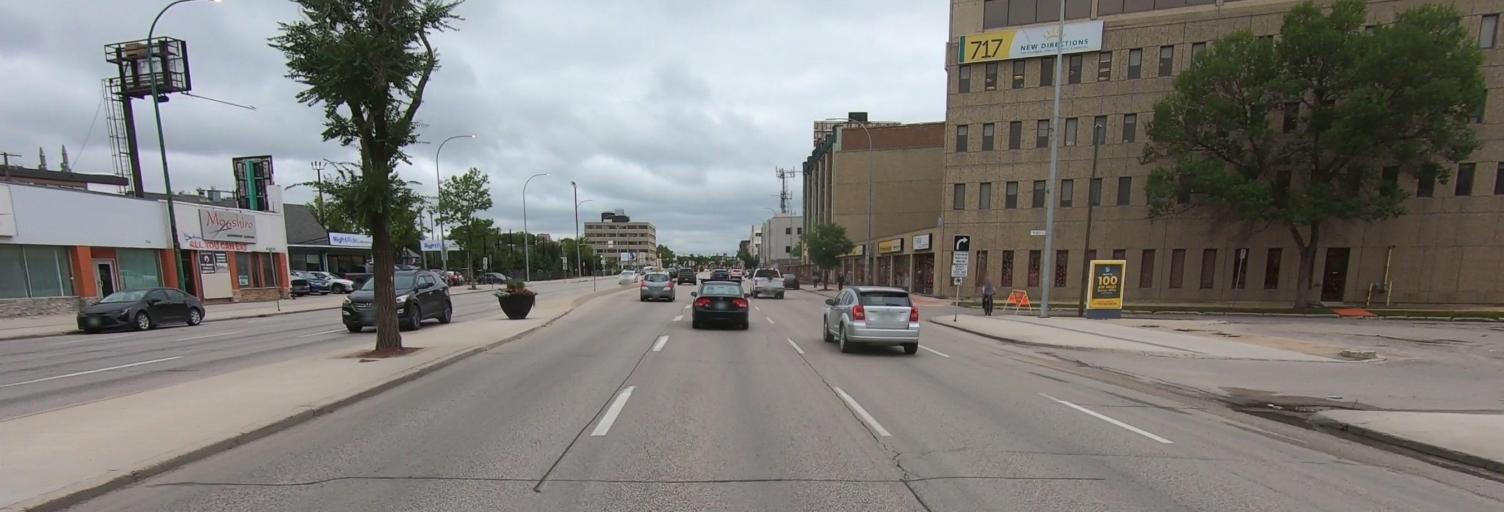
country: CA
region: Manitoba
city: Winnipeg
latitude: 49.8879
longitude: -97.1612
